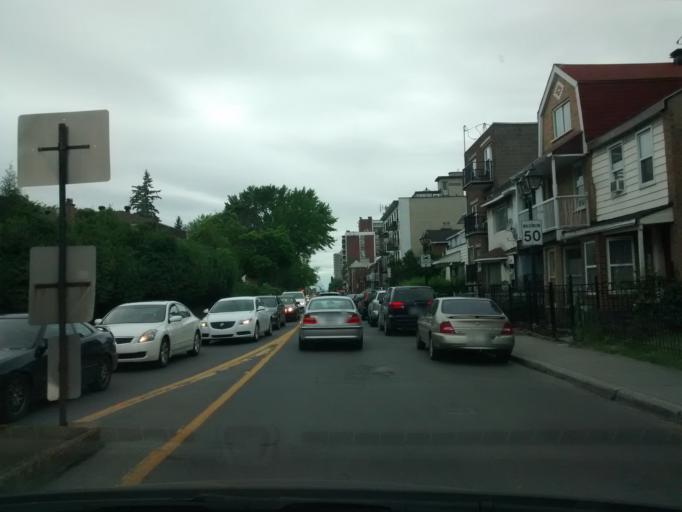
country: CA
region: Quebec
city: Mont-Royal
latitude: 45.5235
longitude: -73.6236
